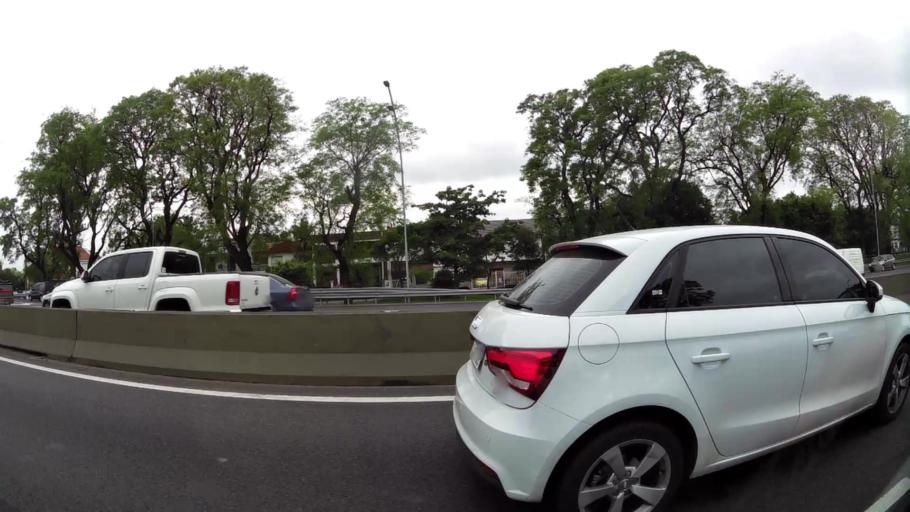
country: AR
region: Buenos Aires
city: Caseros
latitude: -34.6275
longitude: -58.5303
